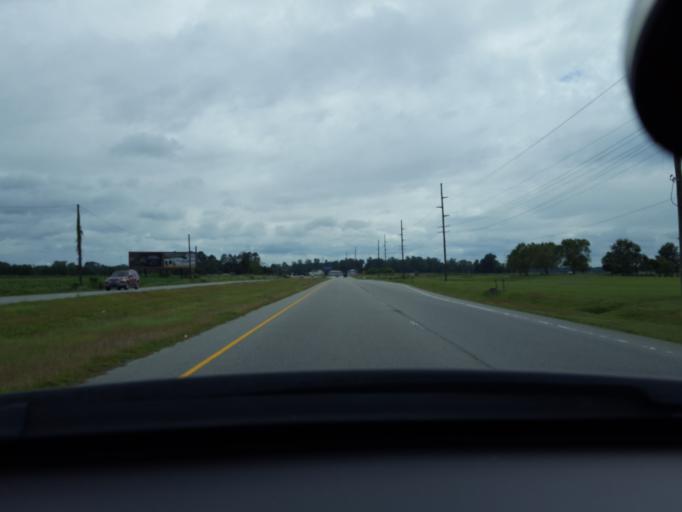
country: US
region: North Carolina
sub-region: Pitt County
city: Ayden
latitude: 35.4455
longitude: -77.4311
